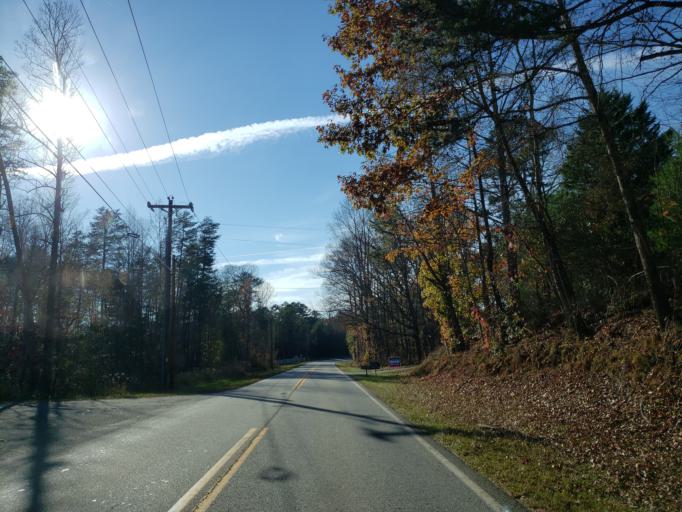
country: US
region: Georgia
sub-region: Lumpkin County
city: Dahlonega
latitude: 34.4656
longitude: -84.0159
